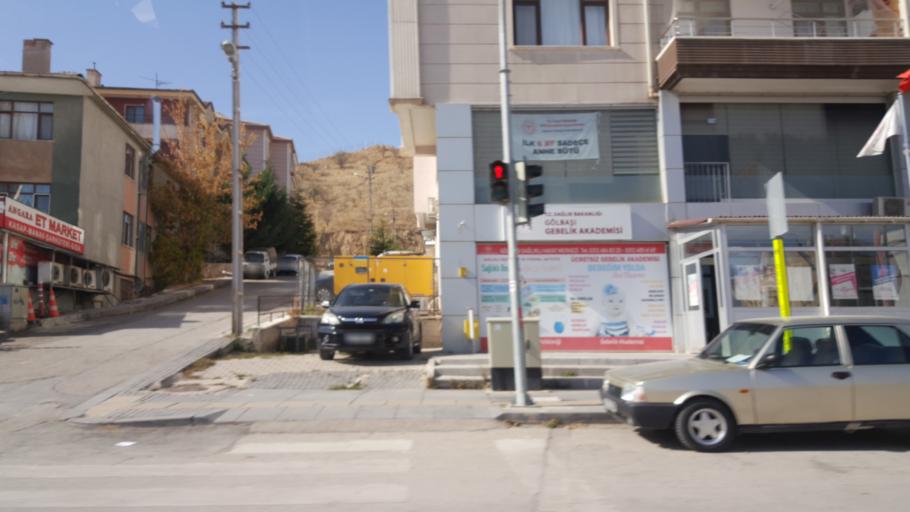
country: TR
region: Ankara
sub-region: Goelbasi
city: Golbasi
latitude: 39.8016
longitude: 32.7987
